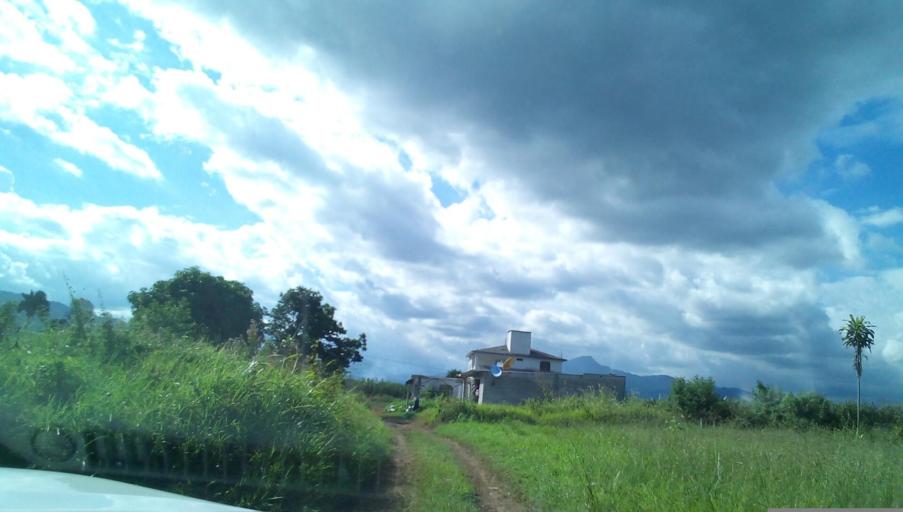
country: MX
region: Veracruz
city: Amatlan de los Reyes
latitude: 18.8262
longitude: -96.9222
